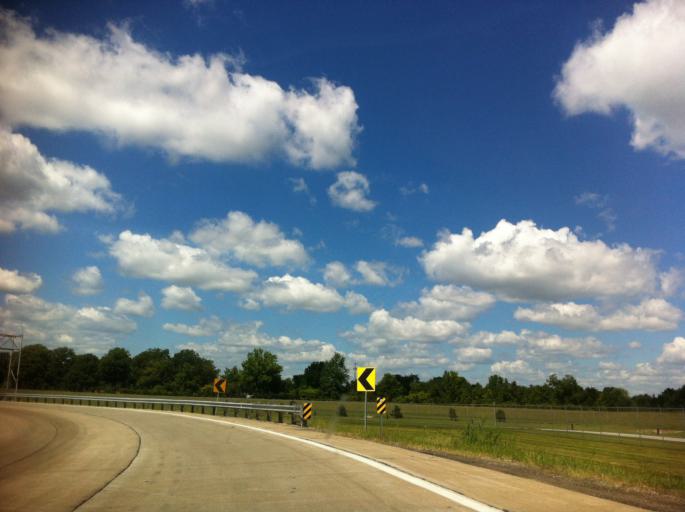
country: US
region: Ohio
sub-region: Wood County
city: Rossford
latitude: 41.5673
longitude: -83.5743
